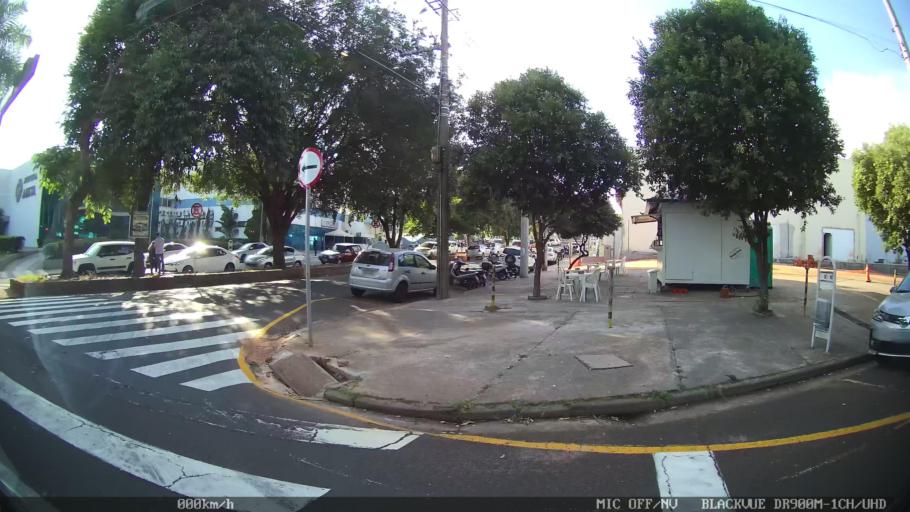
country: BR
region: Sao Paulo
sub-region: Sao Jose Do Rio Preto
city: Sao Jose do Rio Preto
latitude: -20.8234
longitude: -49.3655
